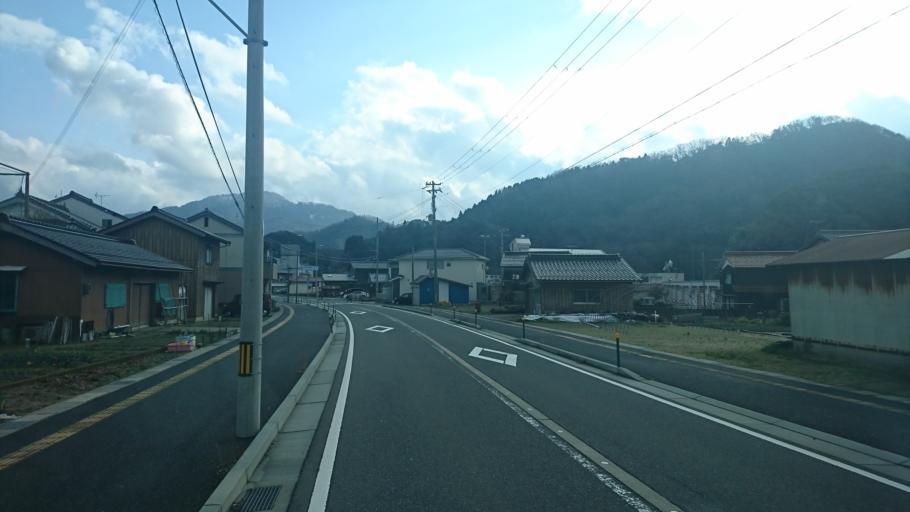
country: JP
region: Tottori
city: Tottori
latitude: 35.6259
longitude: 134.4453
